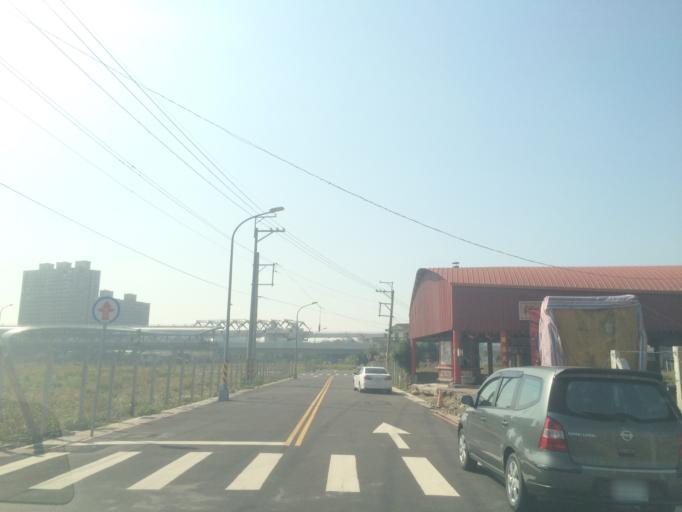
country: TW
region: Taiwan
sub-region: Taichung City
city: Taichung
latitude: 24.1814
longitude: 120.7049
